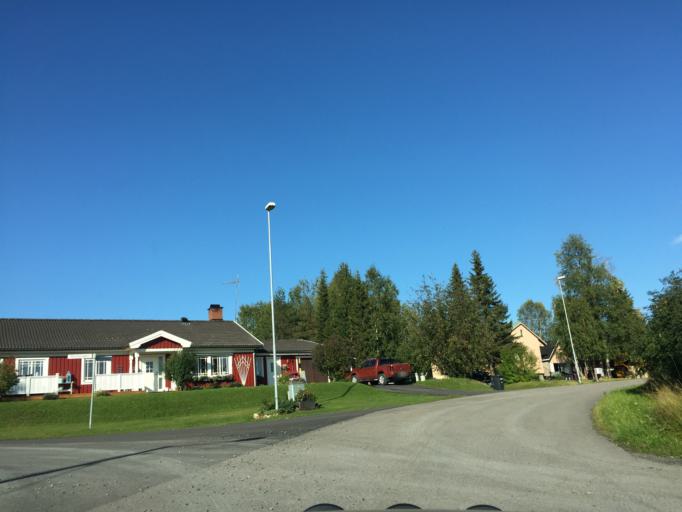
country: SE
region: Norrbotten
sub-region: Gallivare Kommun
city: Malmberget
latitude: 67.6465
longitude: 21.0632
